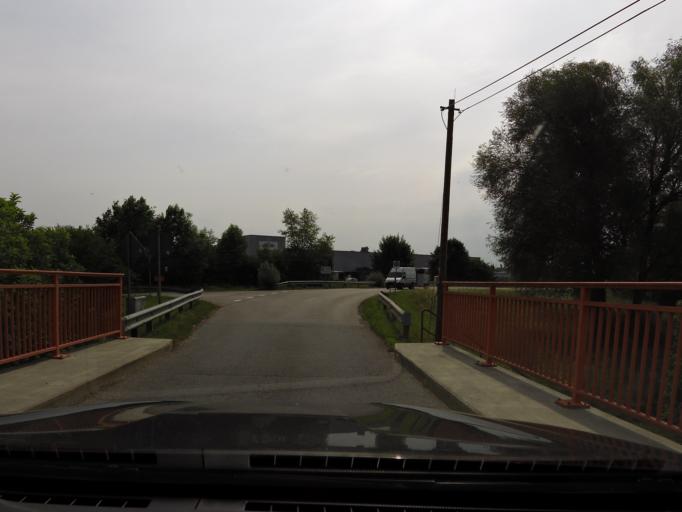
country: DE
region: Bavaria
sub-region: Upper Bavaria
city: Eitting
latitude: 48.3665
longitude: 11.8859
